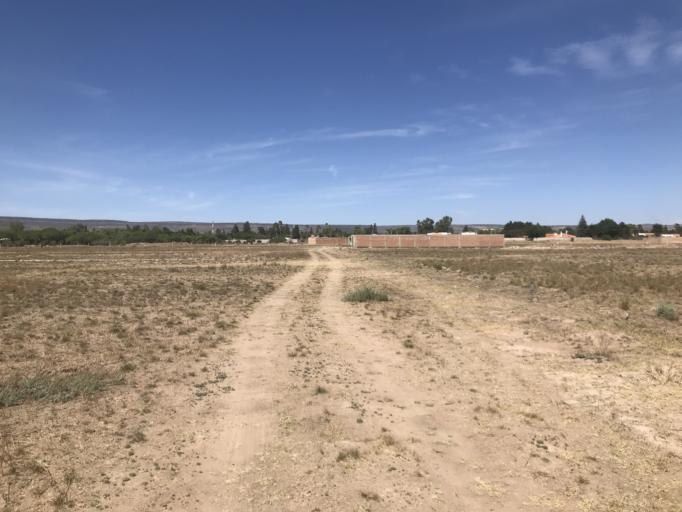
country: MX
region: Durango
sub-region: Durango
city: Sebastian Lerdo de Tejada
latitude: 23.9758
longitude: -104.6557
